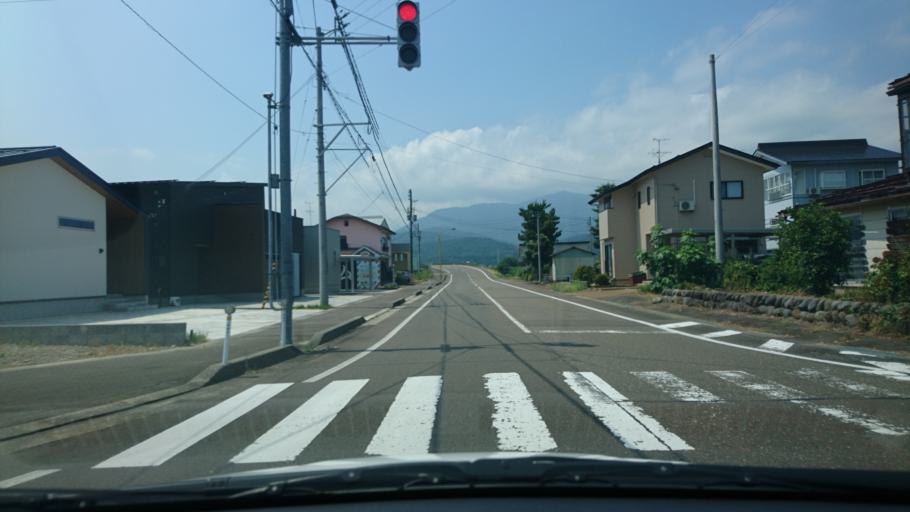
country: JP
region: Niigata
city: Arai
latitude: 37.0534
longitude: 138.2556
